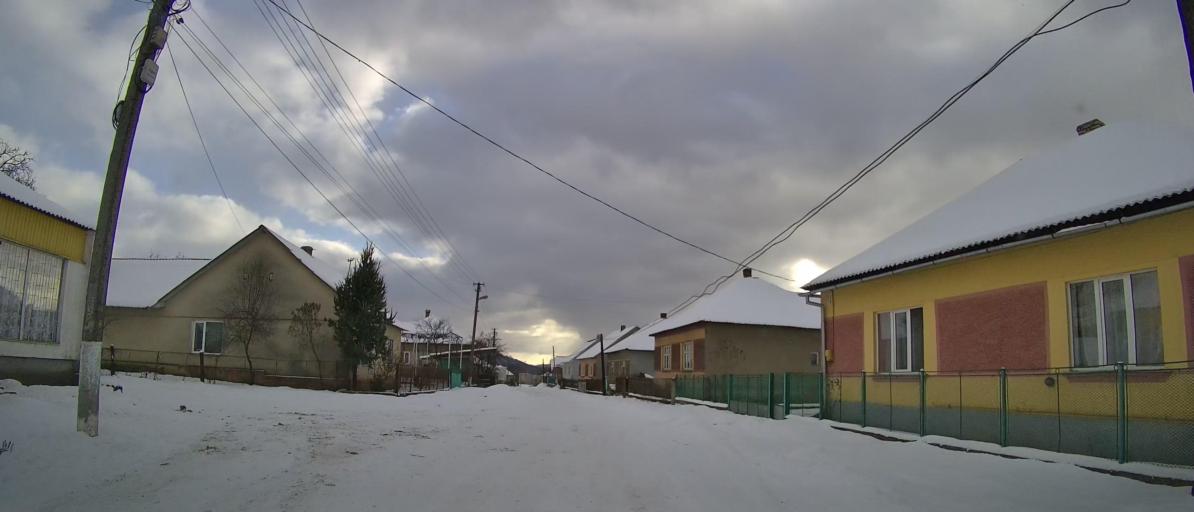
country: UA
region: Zakarpattia
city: Velykyi Bereznyi
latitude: 48.9159
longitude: 22.4641
